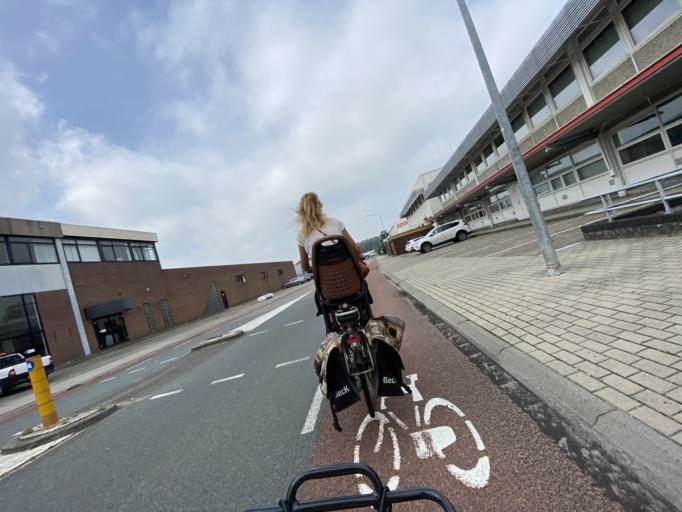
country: NL
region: North Holland
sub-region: Gemeente Amsterdam
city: Driemond
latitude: 52.3139
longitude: 5.0272
